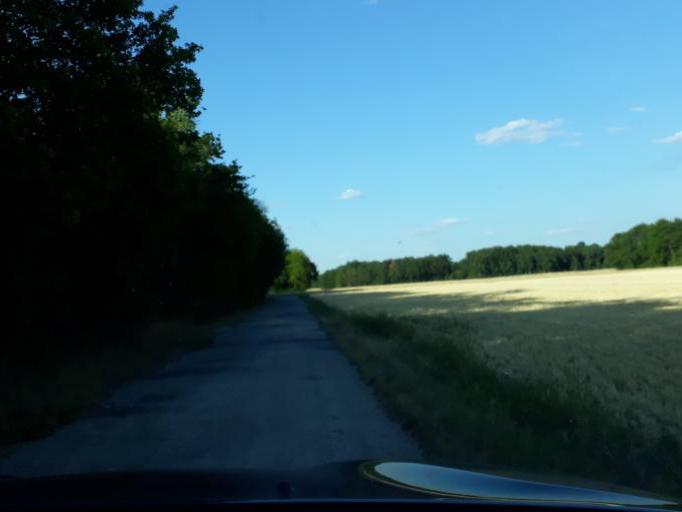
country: FR
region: Centre
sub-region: Departement du Loiret
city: Saint-Ay
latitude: 47.8813
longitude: 1.7338
